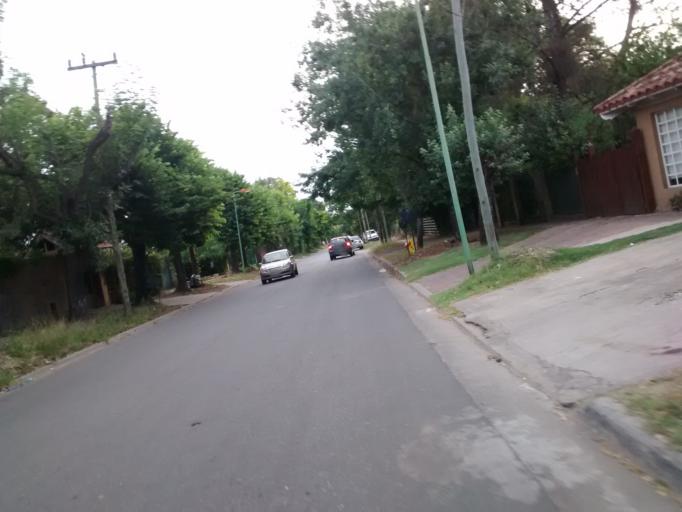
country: AR
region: Buenos Aires
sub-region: Partido de La Plata
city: La Plata
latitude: -34.8775
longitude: -58.0619
